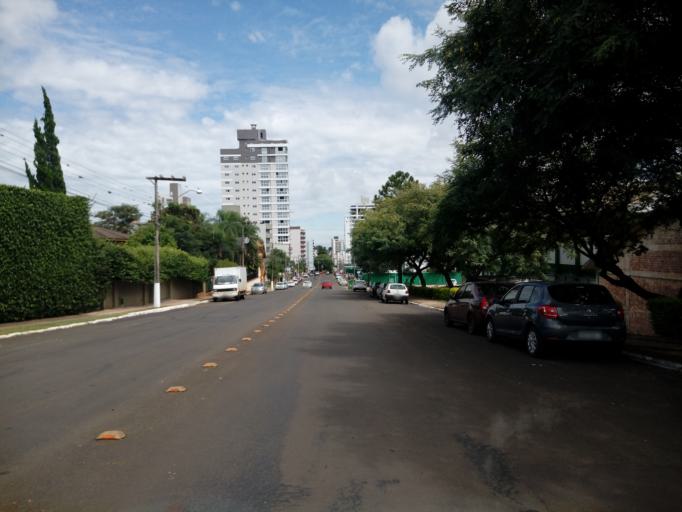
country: BR
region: Santa Catarina
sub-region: Chapeco
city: Chapeco
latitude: -27.1046
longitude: -52.6049
